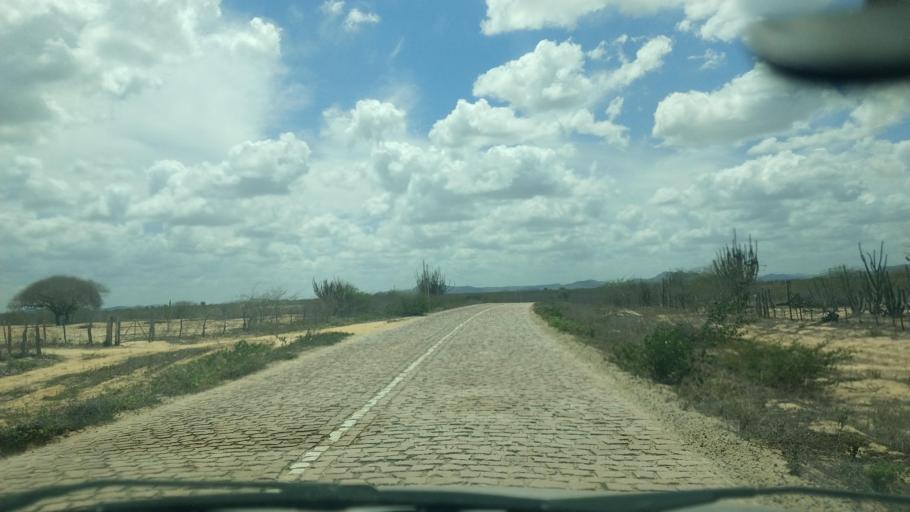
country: BR
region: Rio Grande do Norte
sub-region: Sao Paulo Do Potengi
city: Sao Paulo do Potengi
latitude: -5.9587
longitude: -35.8470
